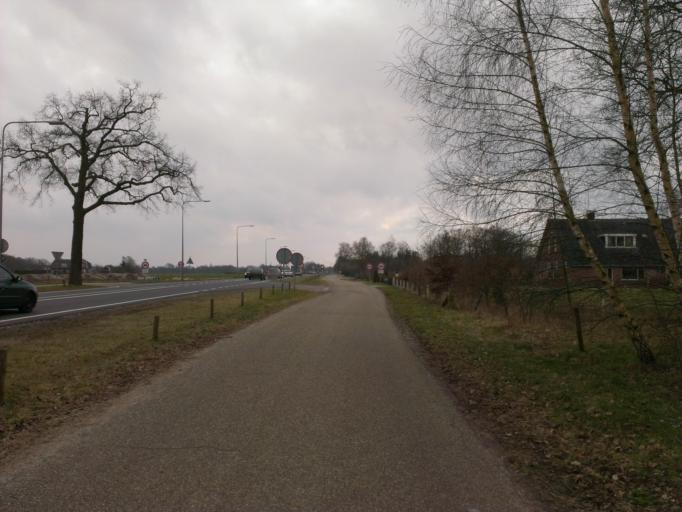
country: NL
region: Overijssel
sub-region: Gemeente Almelo
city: Almelo
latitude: 52.3342
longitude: 6.7039
